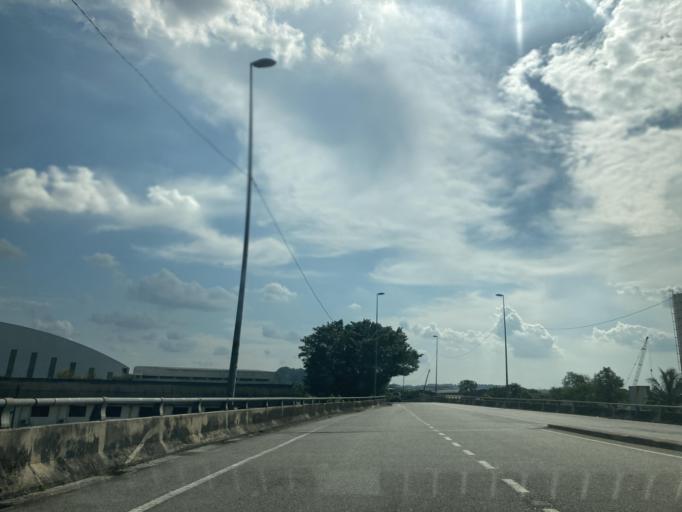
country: MY
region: Selangor
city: Kampung Baru Subang
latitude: 3.1402
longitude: 101.5518
